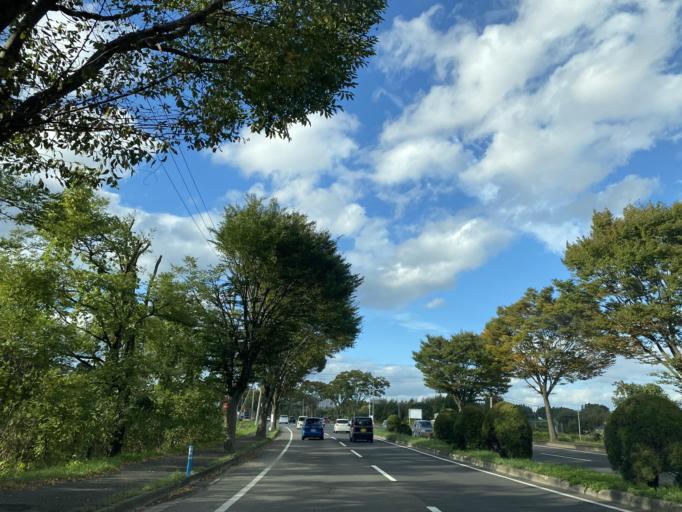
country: JP
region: Miyagi
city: Sendai-shi
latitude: 38.3230
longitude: 140.8444
